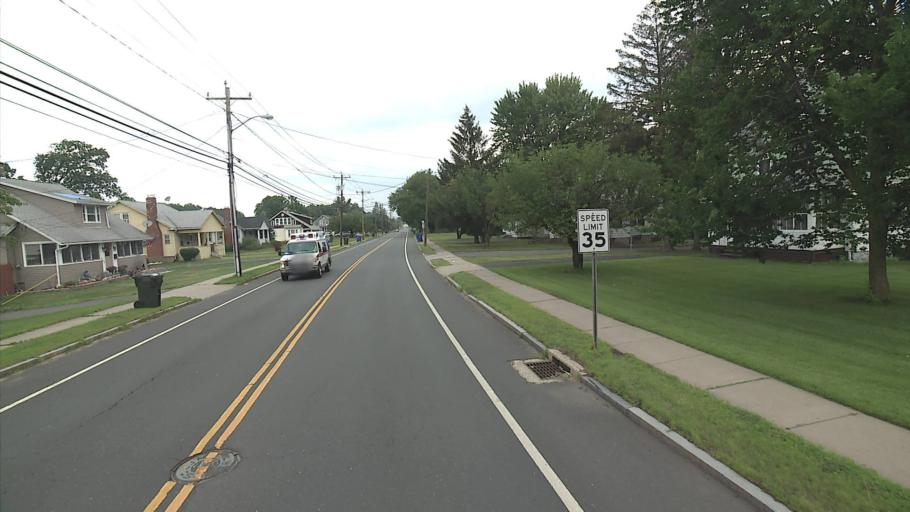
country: US
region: Connecticut
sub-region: Hartford County
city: Newington
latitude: 41.7214
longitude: -72.7365
